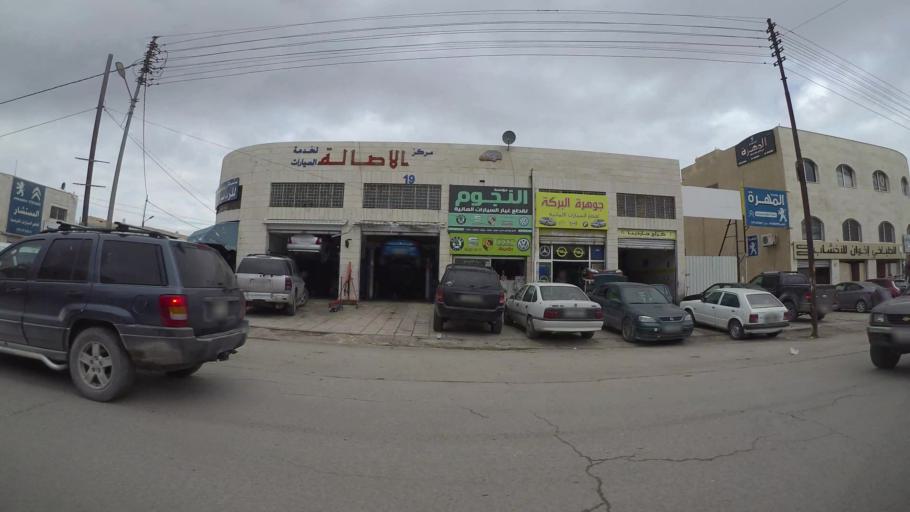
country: JO
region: Amman
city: Wadi as Sir
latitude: 31.9434
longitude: 35.8389
